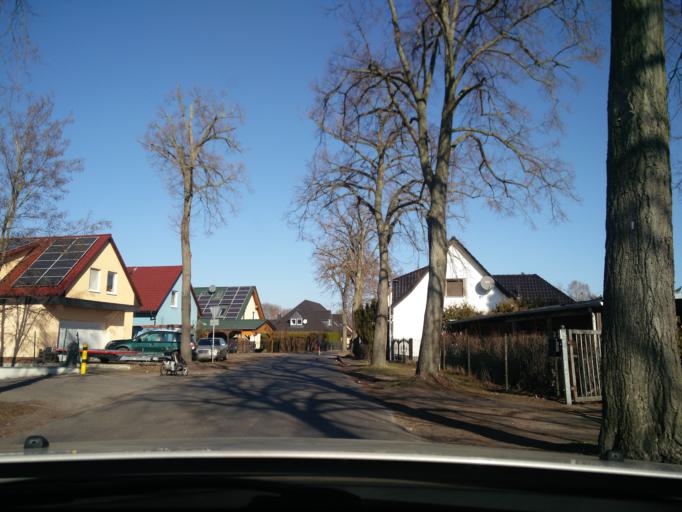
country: DE
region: Brandenburg
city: Brieselang
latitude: 52.5767
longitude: 12.9966
